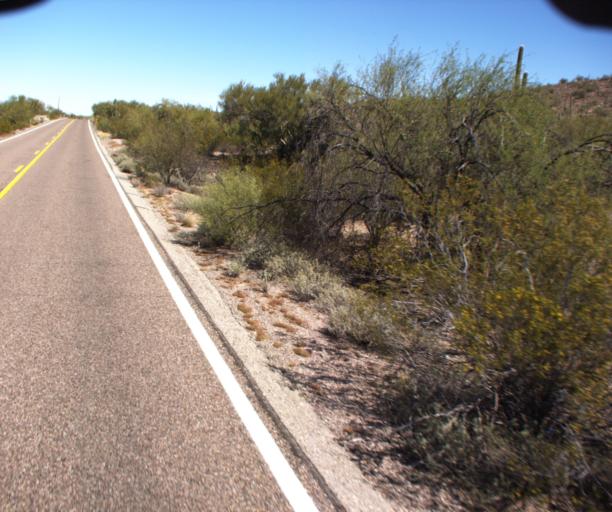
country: MX
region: Sonora
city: Sonoyta
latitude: 32.0063
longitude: -112.8057
